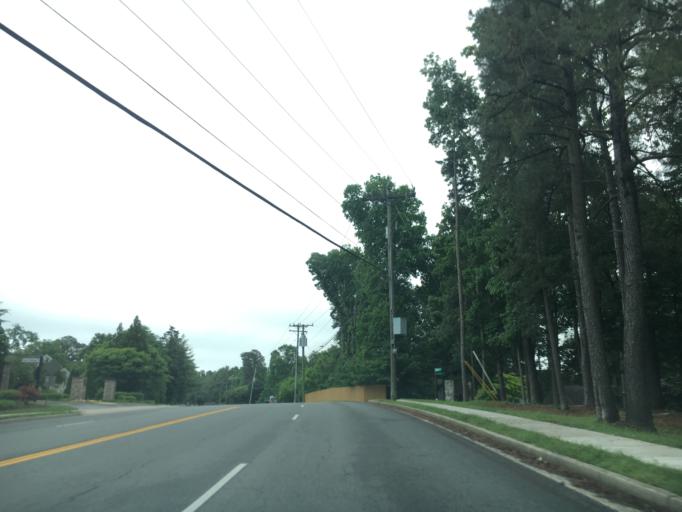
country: US
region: Virginia
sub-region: Henrico County
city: Short Pump
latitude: 37.6326
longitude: -77.6246
